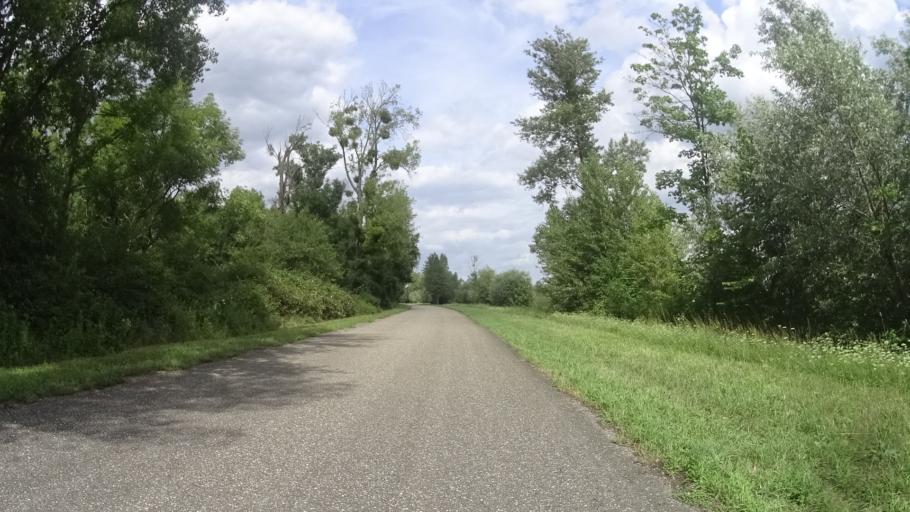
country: DE
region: Baden-Wuerttemberg
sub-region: Karlsruhe Region
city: Rheinmuenster
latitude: 48.7630
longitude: 8.0141
